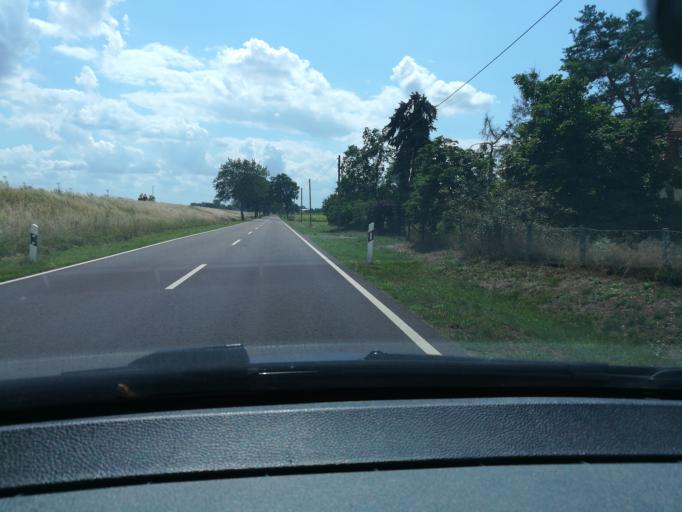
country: DE
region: Saxony-Anhalt
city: Rogatz
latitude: 52.3394
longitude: 11.7806
